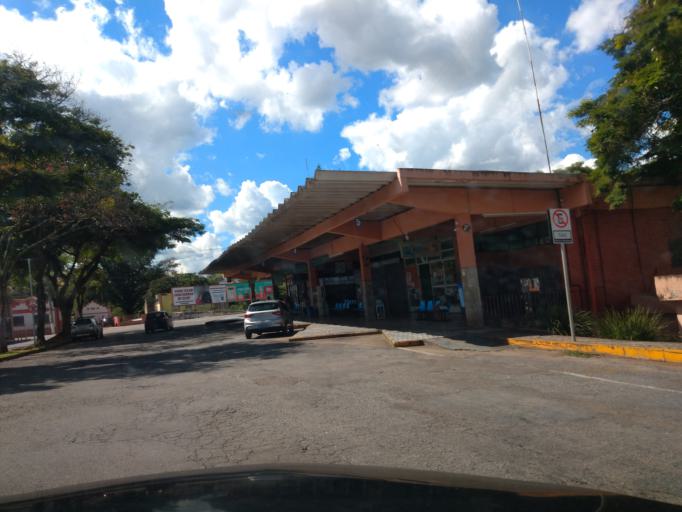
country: BR
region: Minas Gerais
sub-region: Tres Coracoes
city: Tres Coracoes
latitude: -21.7005
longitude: -45.2598
